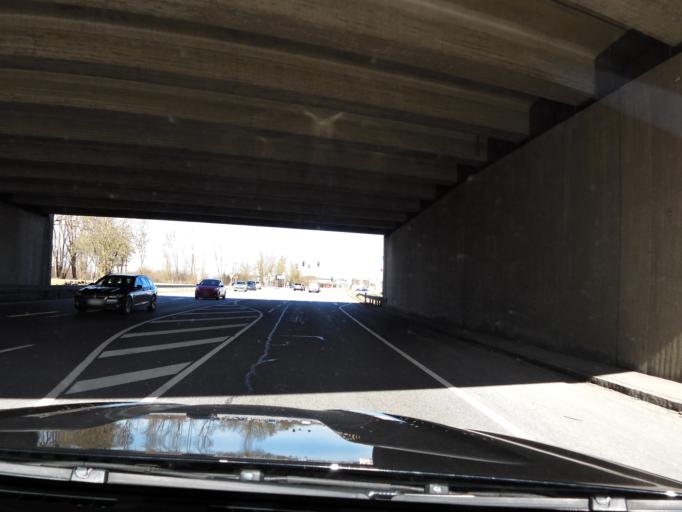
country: DE
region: Bavaria
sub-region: Lower Bavaria
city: Ergolding
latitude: 48.5857
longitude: 12.1885
